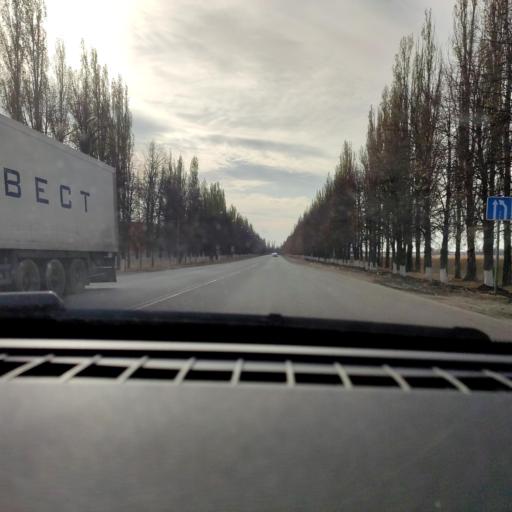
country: RU
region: Voronezj
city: Podgornoye
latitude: 51.8067
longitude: 39.2171
